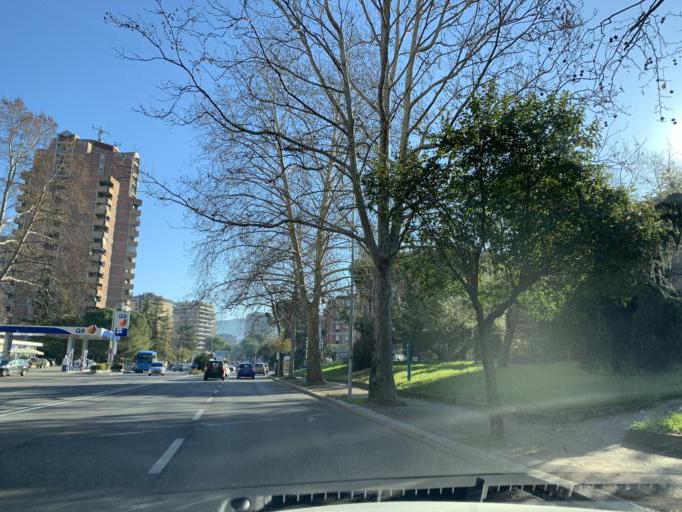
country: IT
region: Umbria
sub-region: Provincia di Terni
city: Terni
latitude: 42.5522
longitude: 12.6400
